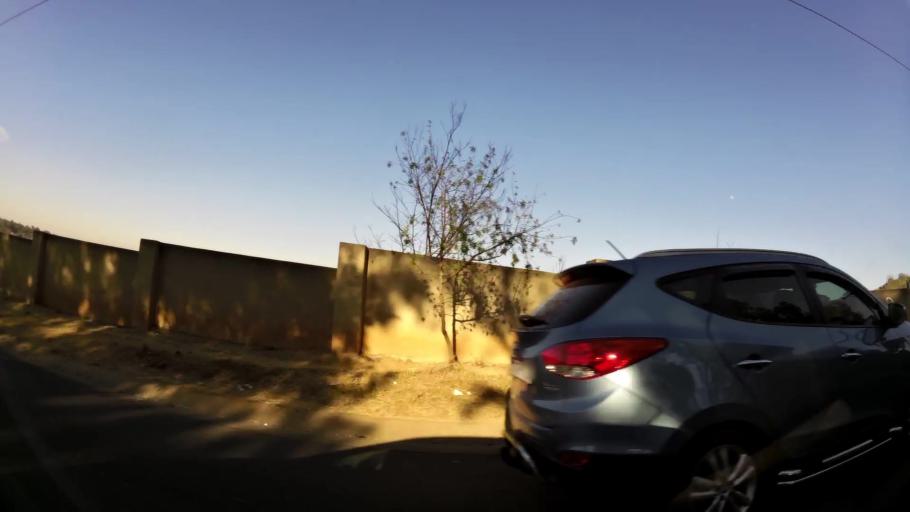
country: ZA
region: Gauteng
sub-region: City of Johannesburg Metropolitan Municipality
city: Midrand
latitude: -26.0170
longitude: 28.1401
